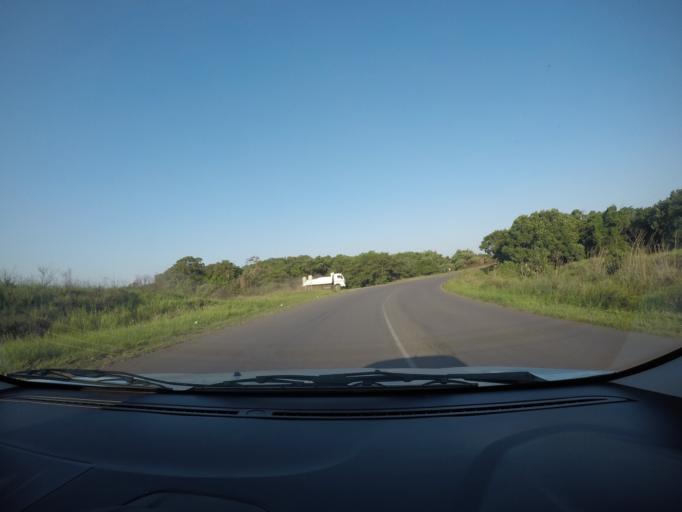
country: ZA
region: KwaZulu-Natal
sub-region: uThungulu District Municipality
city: Richards Bay
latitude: -28.7478
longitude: 32.0126
